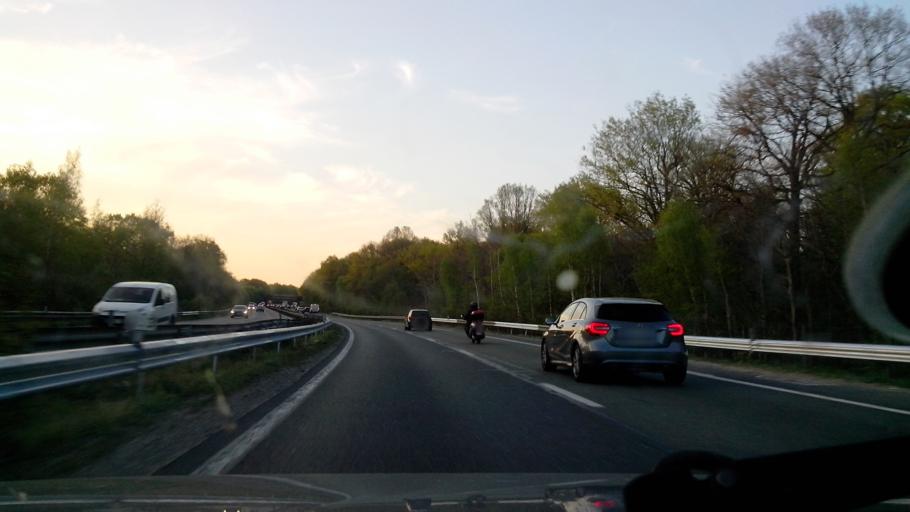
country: FR
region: Ile-de-France
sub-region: Departement de Seine-et-Marne
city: Lesigny
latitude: 48.7630
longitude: 2.6159
